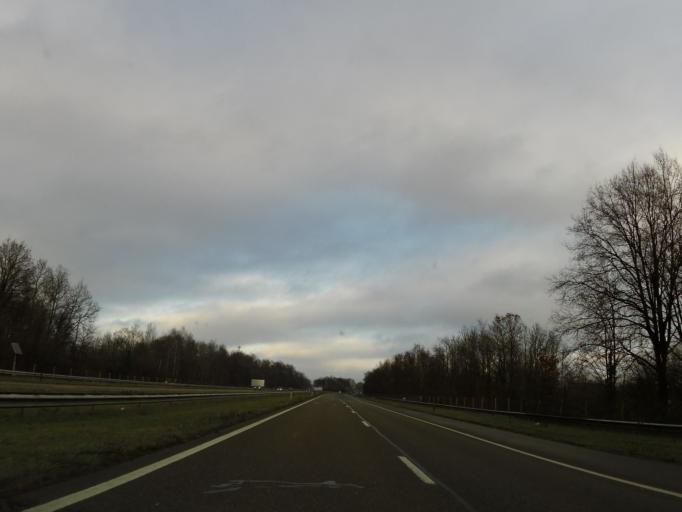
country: NL
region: Limburg
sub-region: Valkenburg aan de Geul
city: Valkenburg
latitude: 50.8795
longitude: 5.8339
